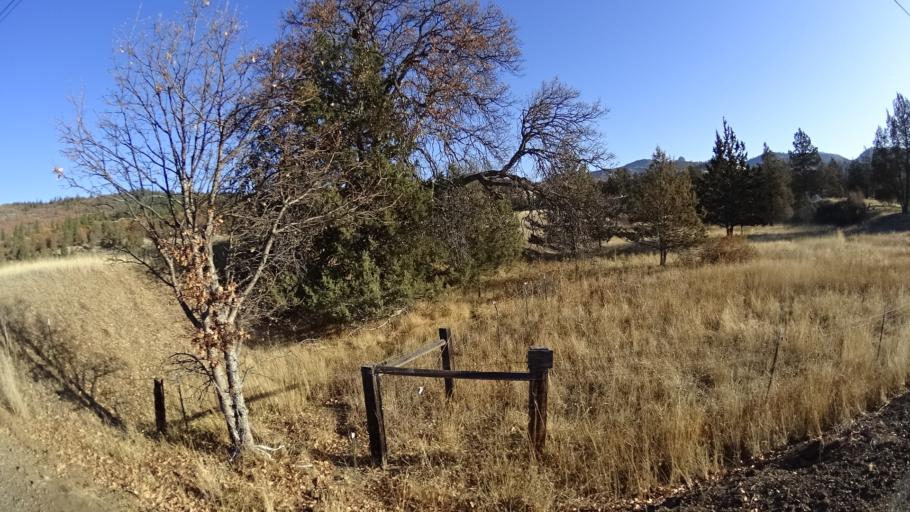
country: US
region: Oregon
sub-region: Jackson County
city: Ashland
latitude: 41.9997
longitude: -122.6344
